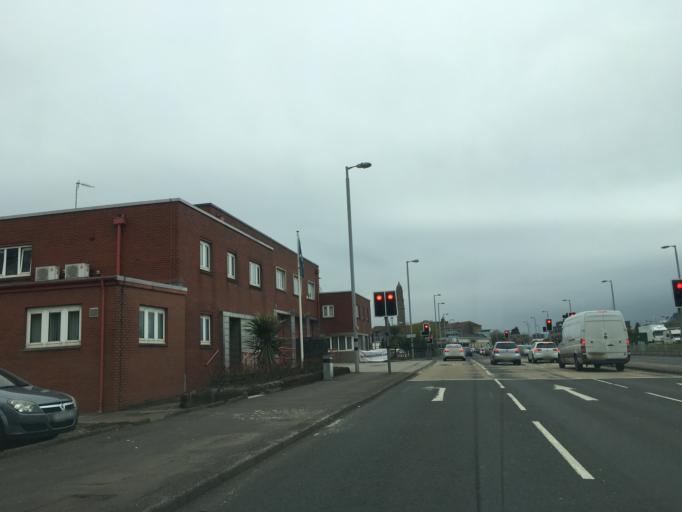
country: GB
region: Scotland
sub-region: Inverclyde
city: Greenock
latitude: 55.9443
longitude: -4.7469
